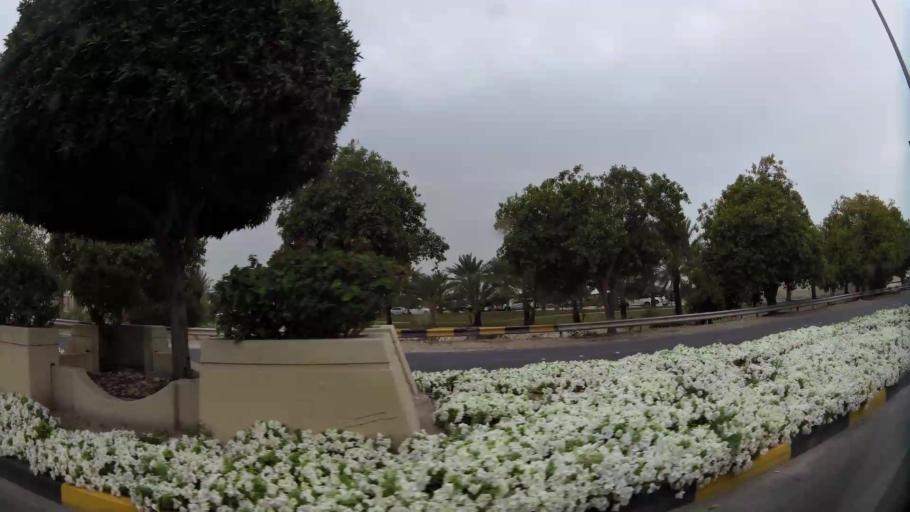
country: BH
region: Northern
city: Ar Rifa'
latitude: 26.1450
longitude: 50.5432
